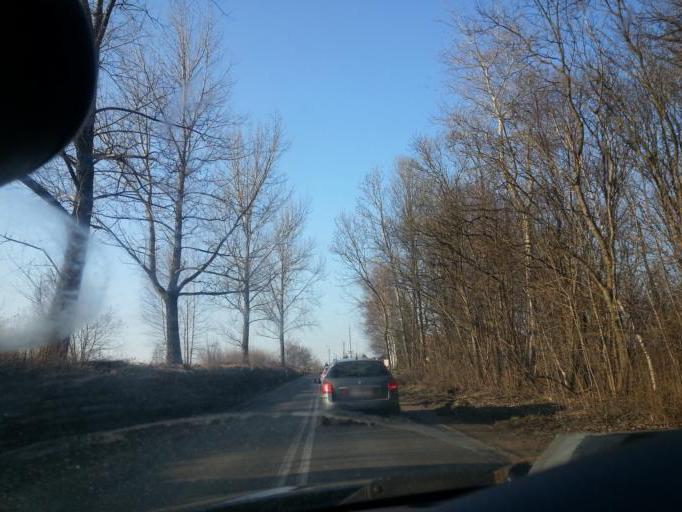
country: PL
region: Lower Silesian Voivodeship
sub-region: Powiat jeleniogorski
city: Myslakowice
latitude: 50.8440
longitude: 15.7866
